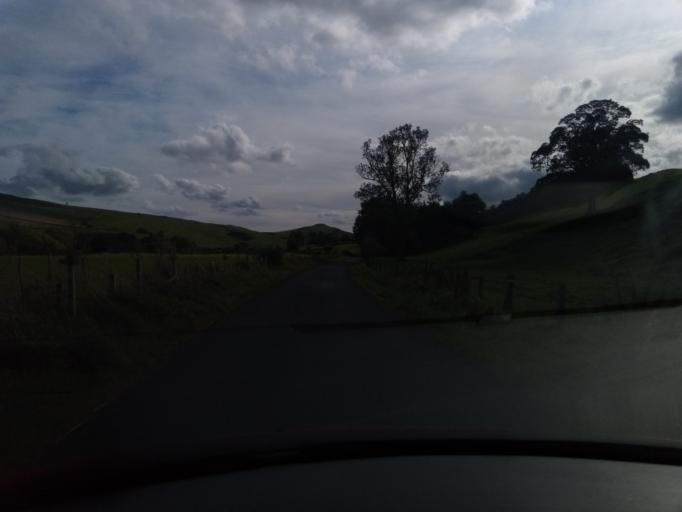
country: GB
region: Scotland
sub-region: The Scottish Borders
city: Kelso
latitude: 55.4907
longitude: -2.3479
